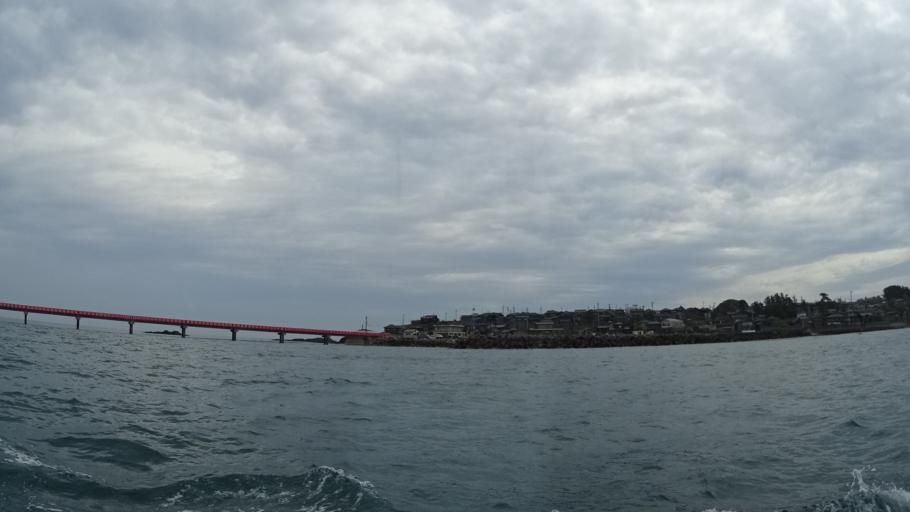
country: JP
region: Fukui
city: Mikuni
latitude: 36.2487
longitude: 136.1207
